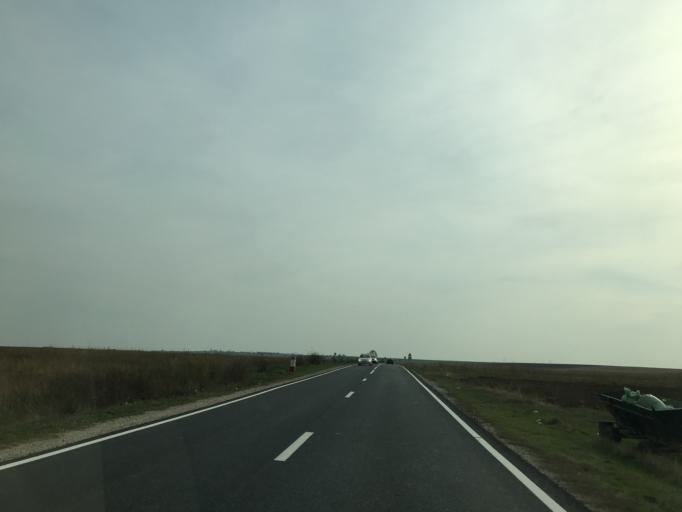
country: RO
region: Olt
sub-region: Comuna Piatra Olt
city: Piatra
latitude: 44.3436
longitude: 24.2955
